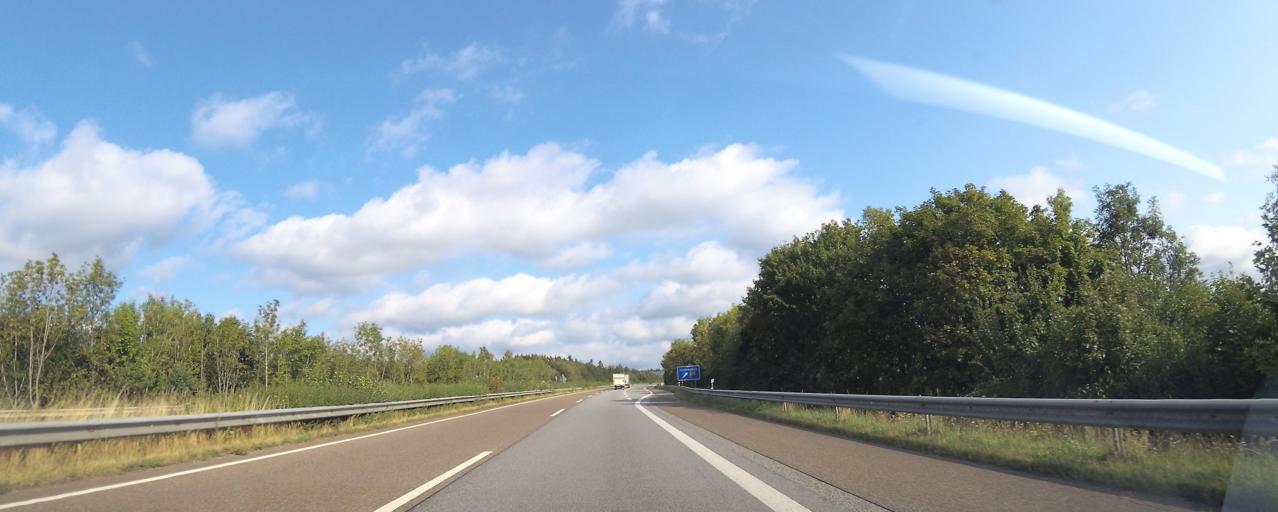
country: DE
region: Rheinland-Pfalz
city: Hermeskeil
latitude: 49.6558
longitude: 6.9242
